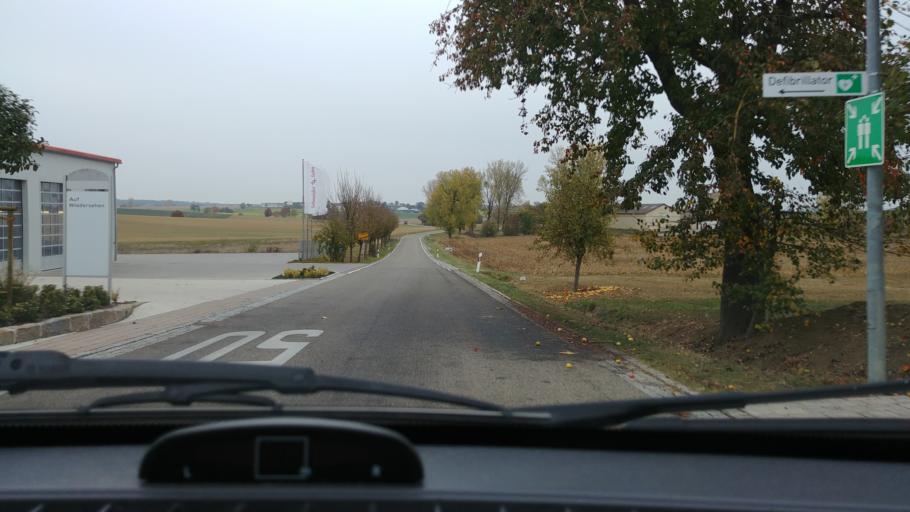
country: DE
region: Bavaria
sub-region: Regierungsbezirk Mittelfranken
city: Insingen
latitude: 49.3154
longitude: 10.0939
